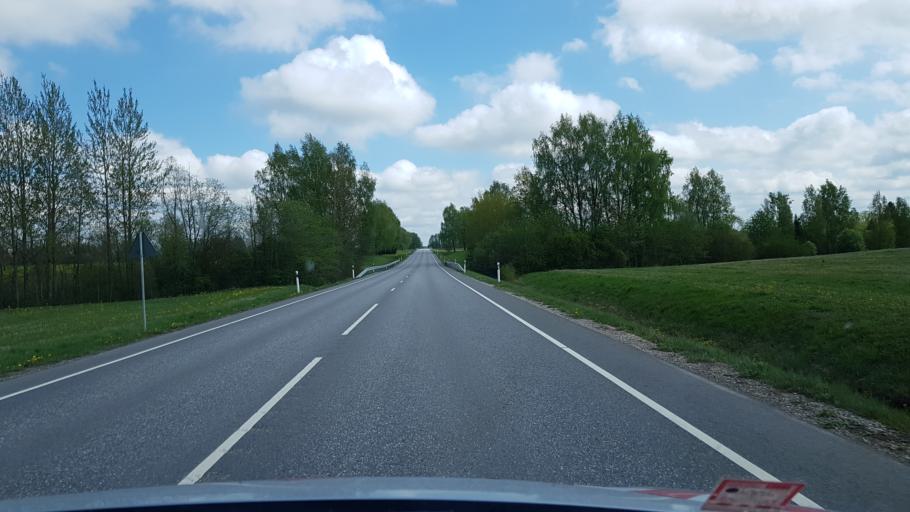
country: EE
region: Viljandimaa
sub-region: Karksi vald
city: Karksi-Nuia
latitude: 58.1210
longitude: 25.4846
